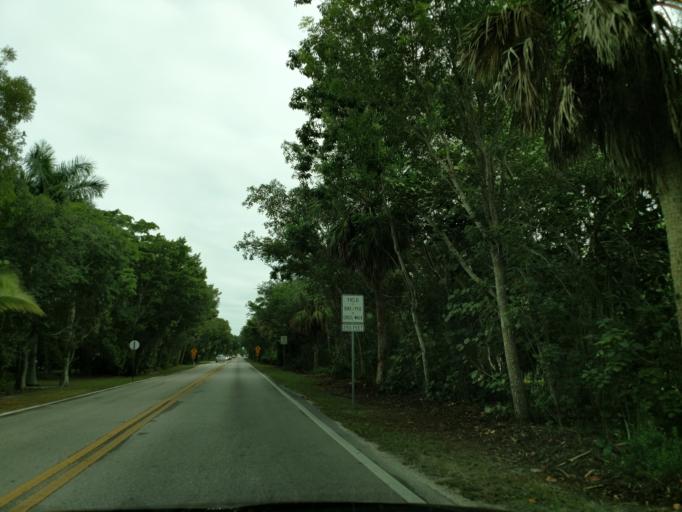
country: US
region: Florida
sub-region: Lee County
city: Sanibel
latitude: 26.4433
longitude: -82.0520
